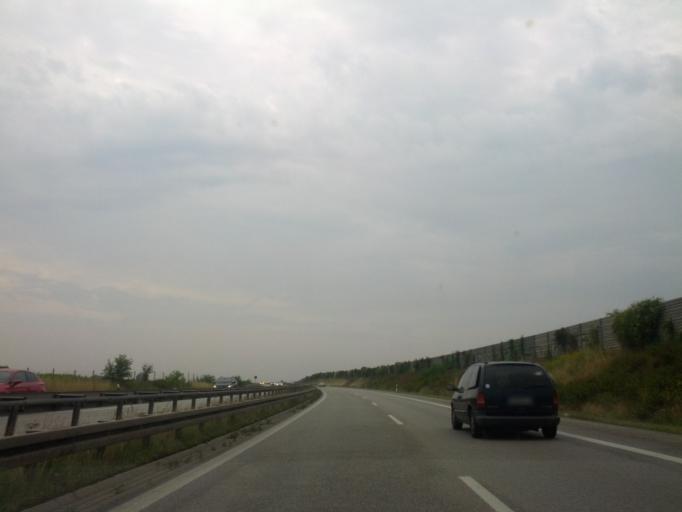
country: DE
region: Mecklenburg-Vorpommern
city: Kritzmow
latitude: 54.0796
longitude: 12.0568
